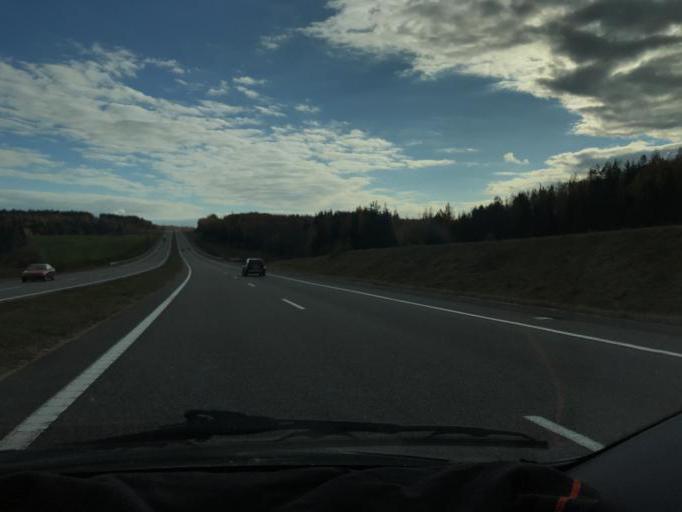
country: BY
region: Minsk
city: Lahoysk
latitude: 54.1894
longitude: 27.8156
